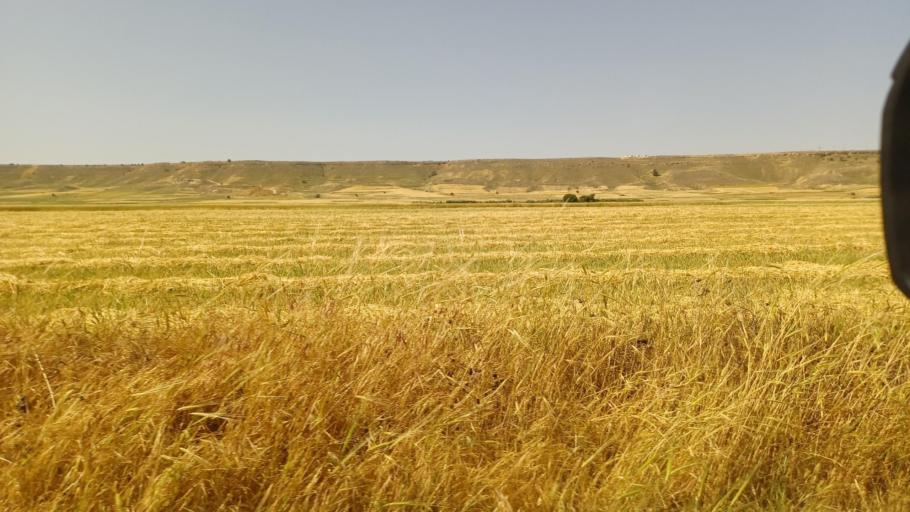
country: CY
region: Lefkosia
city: Mammari
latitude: 35.1798
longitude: 33.2259
